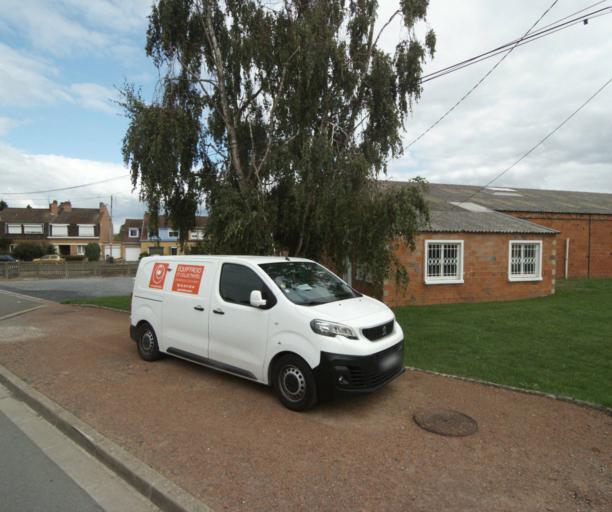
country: FR
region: Nord-Pas-de-Calais
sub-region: Departement du Nord
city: Anstaing
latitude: 50.6090
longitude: 3.1901
